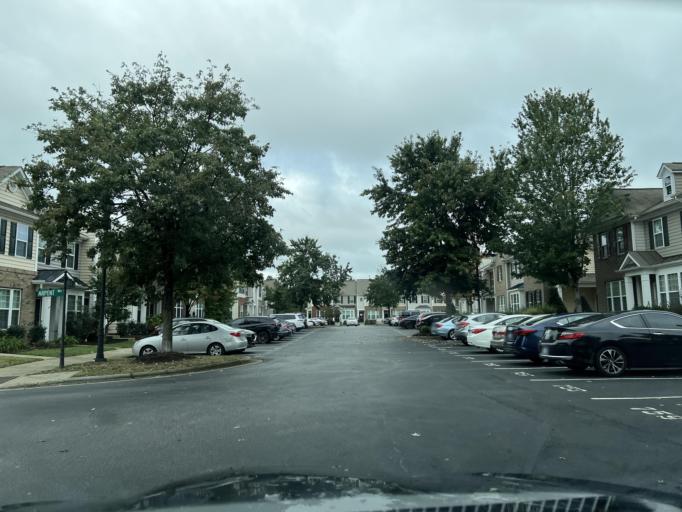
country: US
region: North Carolina
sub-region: Wake County
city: Raleigh
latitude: 35.7319
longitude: -78.6593
